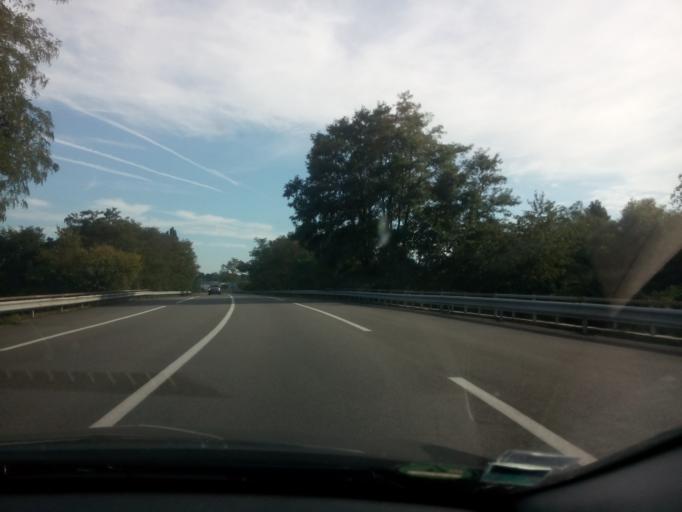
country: FR
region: Alsace
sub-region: Departement du Bas-Rhin
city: Wissembourg
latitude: 49.0260
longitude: 7.9638
